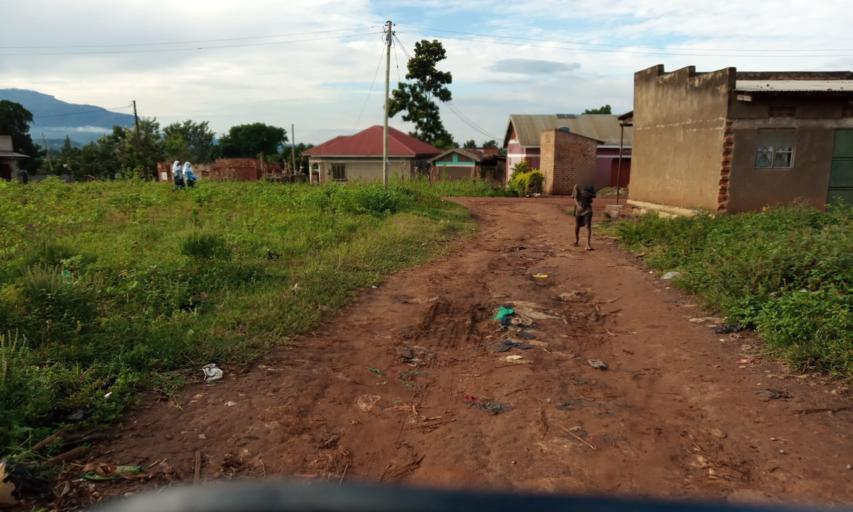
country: UG
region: Eastern Region
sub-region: Mbale District
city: Mbale
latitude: 1.1405
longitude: 34.1685
